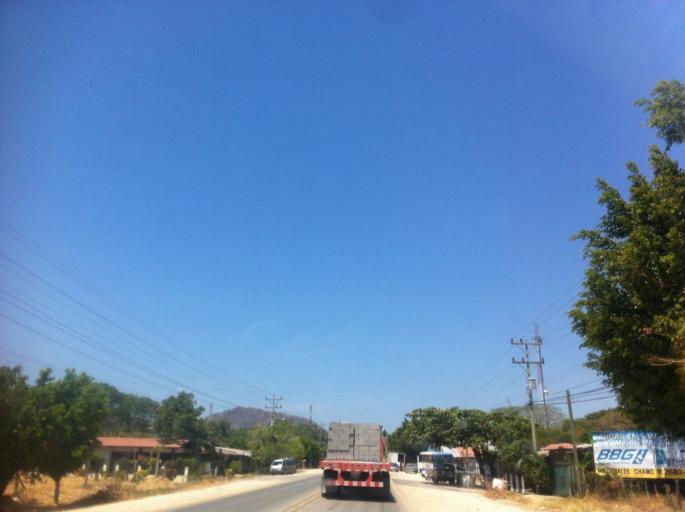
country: CR
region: Guanacaste
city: Santa Cruz
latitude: 10.2686
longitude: -85.5805
